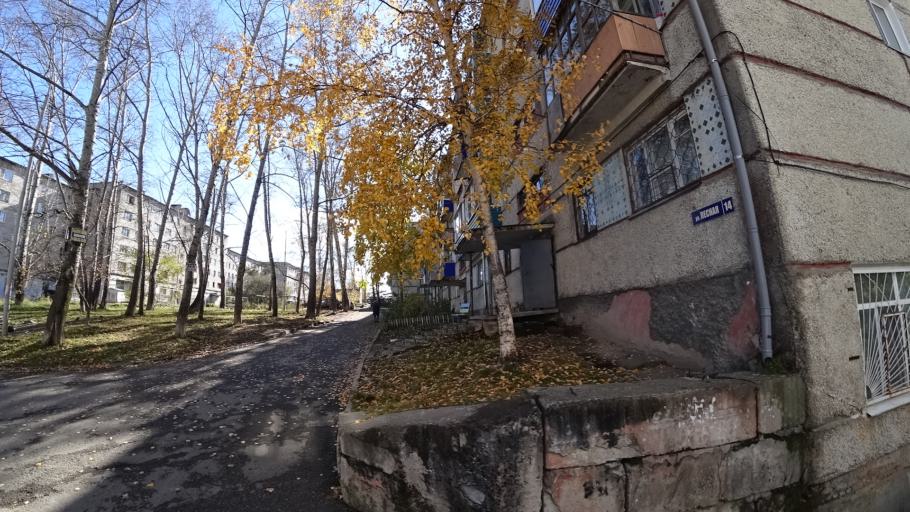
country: RU
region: Khabarovsk Krai
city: Amursk
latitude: 50.2216
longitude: 136.9017
